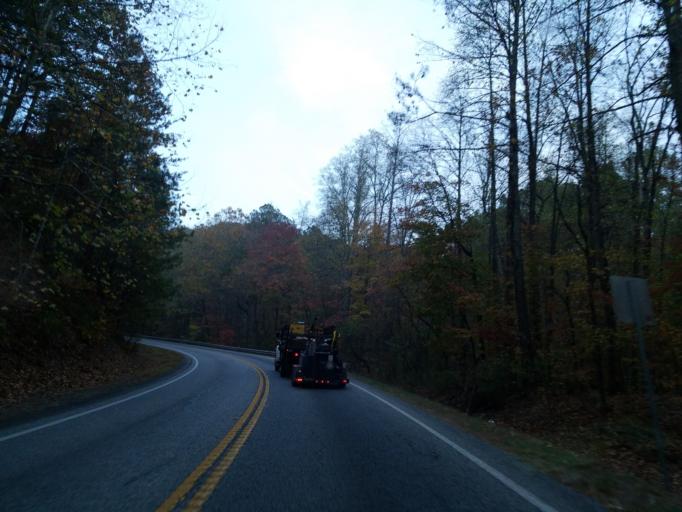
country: US
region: Georgia
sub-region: Gilmer County
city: Ellijay
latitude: 34.5797
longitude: -84.6394
